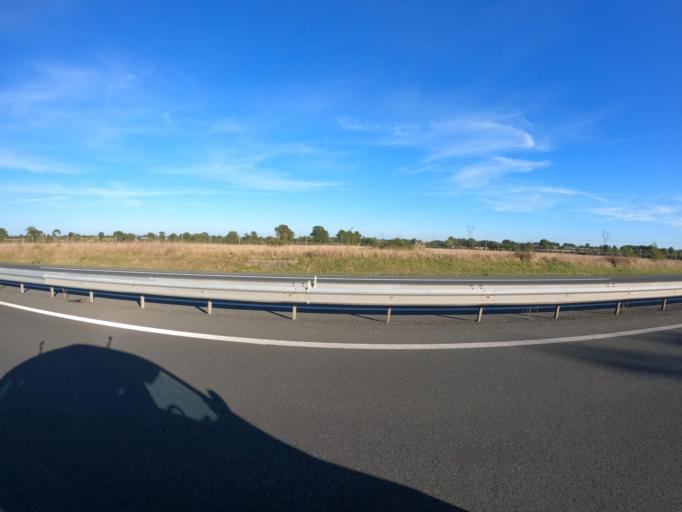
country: FR
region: Pays de la Loire
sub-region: Departement de Maine-et-Loire
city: Saint-Lambert-du-Lattay
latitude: 47.2613
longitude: -0.6159
